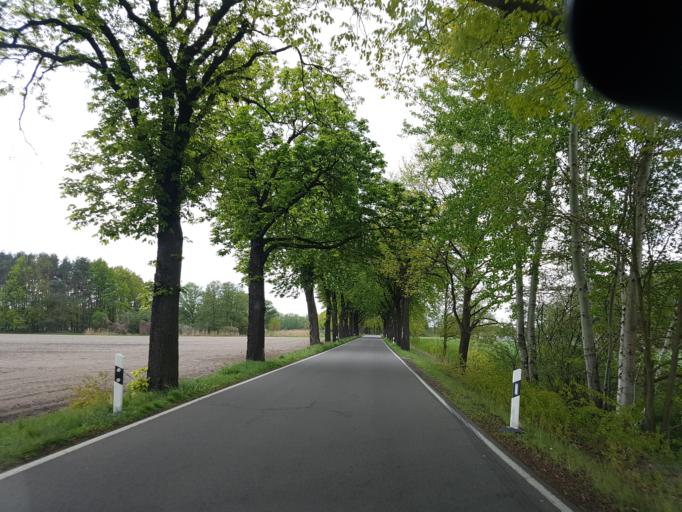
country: DE
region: Brandenburg
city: Bronkow
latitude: 51.6239
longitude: 13.9283
